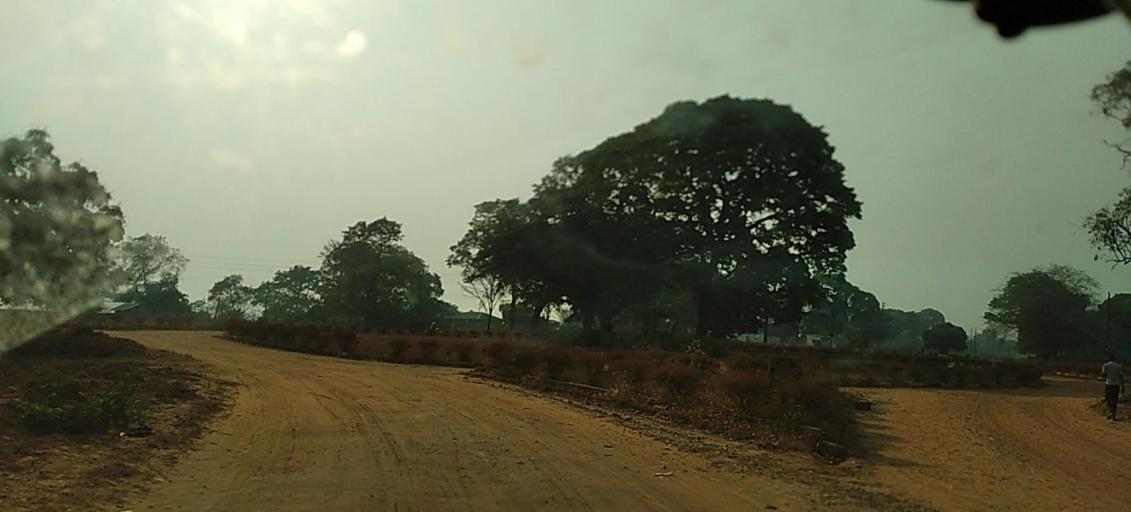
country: ZM
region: North-Western
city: Kabompo
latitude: -13.5982
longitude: 24.2074
